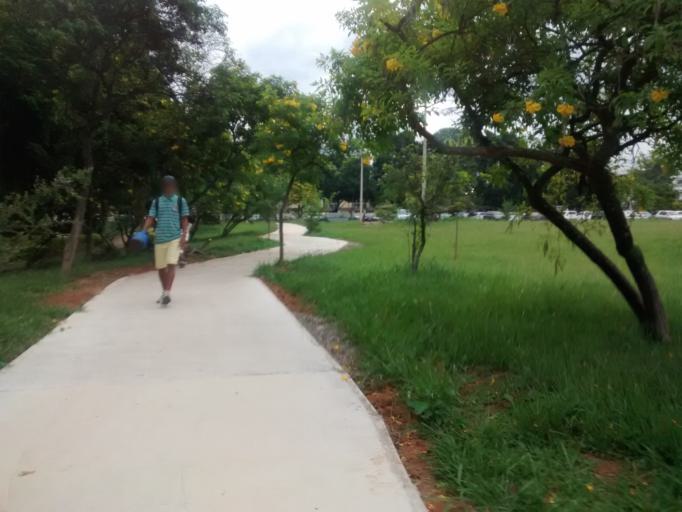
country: BR
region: Federal District
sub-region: Brasilia
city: Brasilia
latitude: -15.7475
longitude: -47.8941
